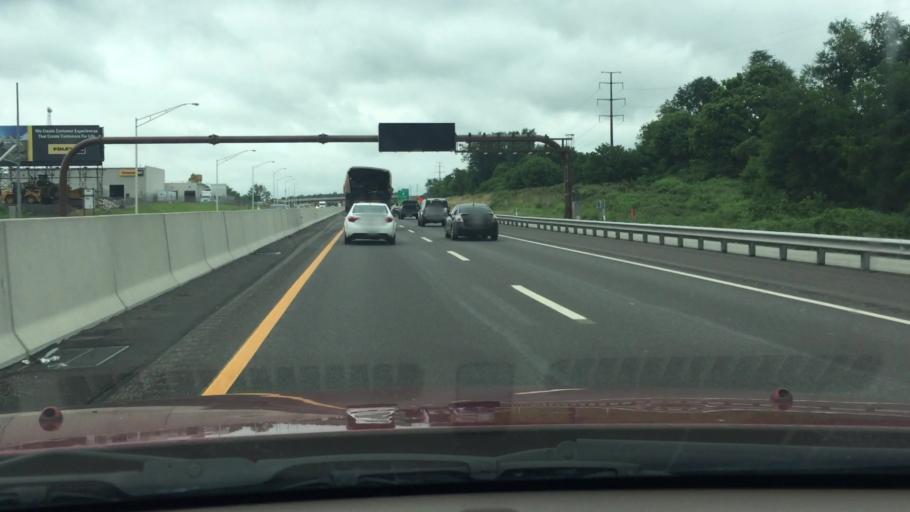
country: US
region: Pennsylvania
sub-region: Bucks County
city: Hulmeville
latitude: 40.1282
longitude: -74.9342
